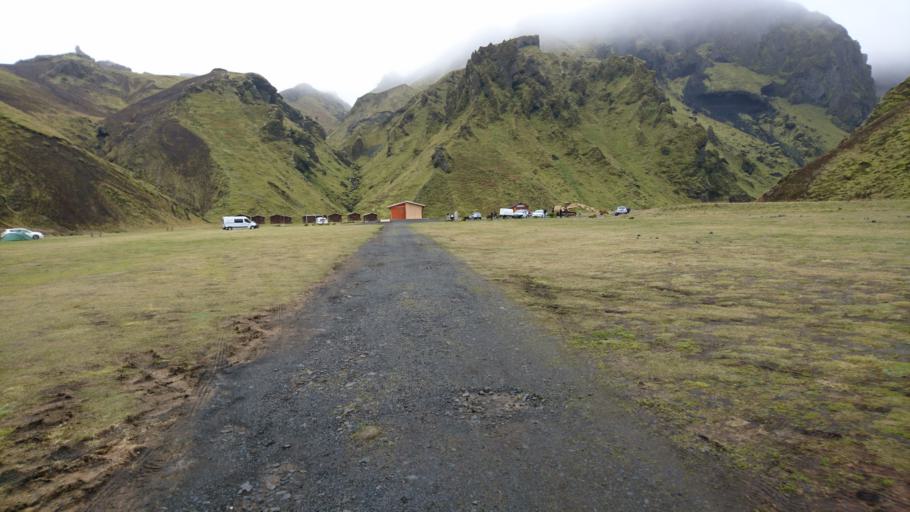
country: IS
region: South
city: Vestmannaeyjar
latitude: 63.5295
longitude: -18.8864
